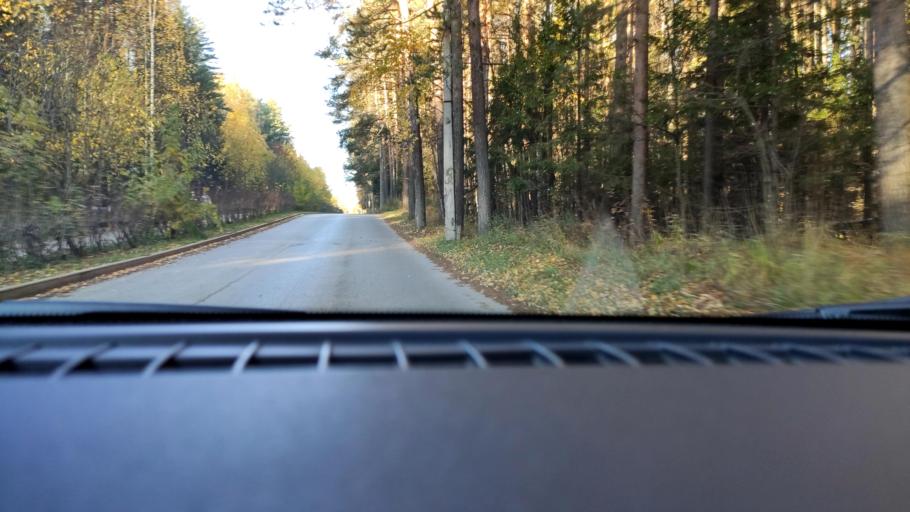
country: RU
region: Perm
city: Perm
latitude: 58.0554
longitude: 56.2223
